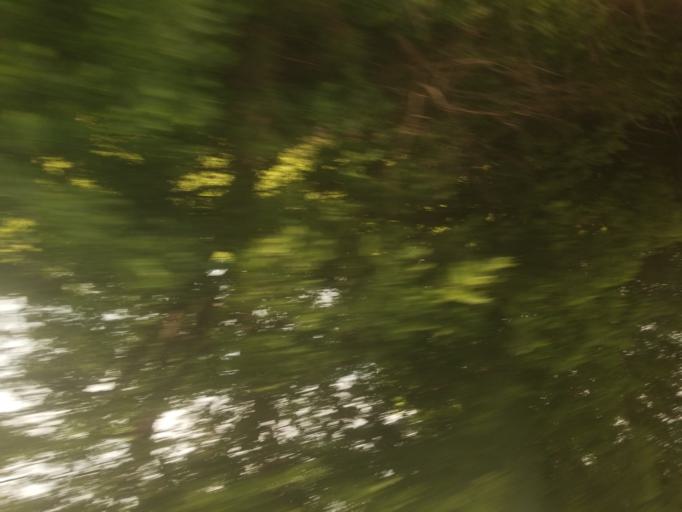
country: US
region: Illinois
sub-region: Henry County
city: Kewanee
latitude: 41.3031
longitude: -89.7396
